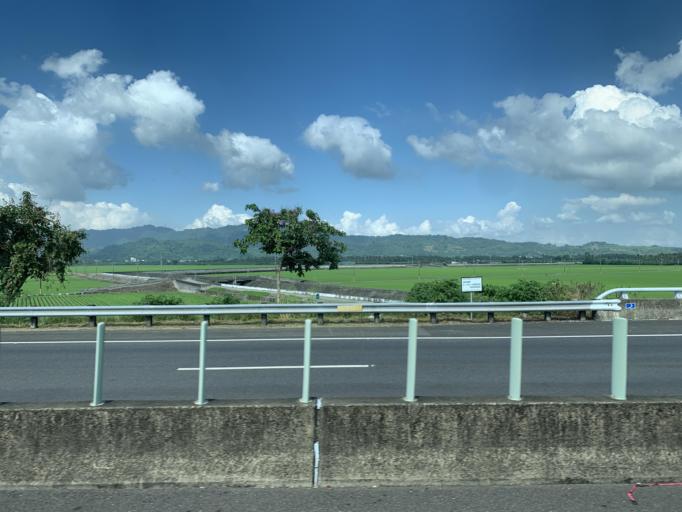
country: TW
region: Taiwan
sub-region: Pingtung
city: Pingtung
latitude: 22.8275
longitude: 120.4890
